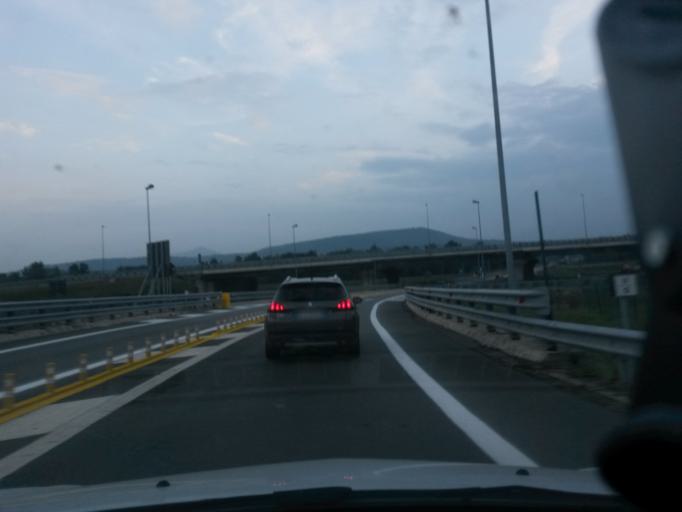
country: IT
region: Piedmont
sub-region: Provincia di Torino
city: Drubiaglio-Grangia
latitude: 45.0926
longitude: 7.4188
